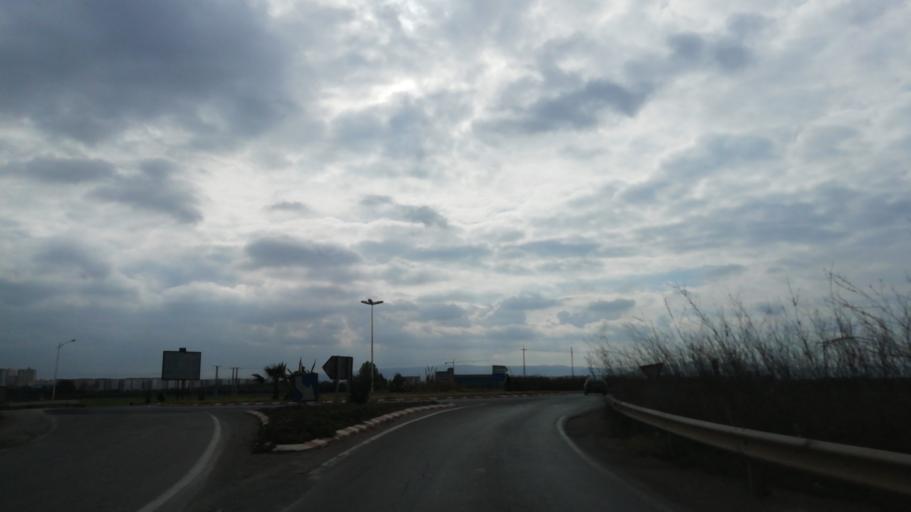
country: DZ
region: Oran
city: Sidi ech Chahmi
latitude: 35.5679
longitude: -0.4500
